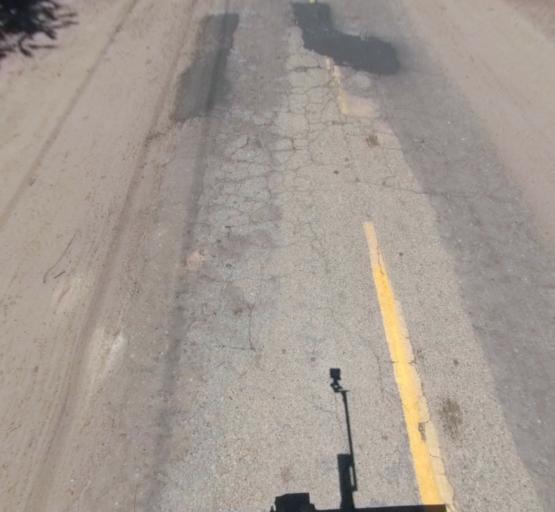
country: US
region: California
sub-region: Madera County
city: Chowchilla
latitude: 37.0545
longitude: -120.2791
